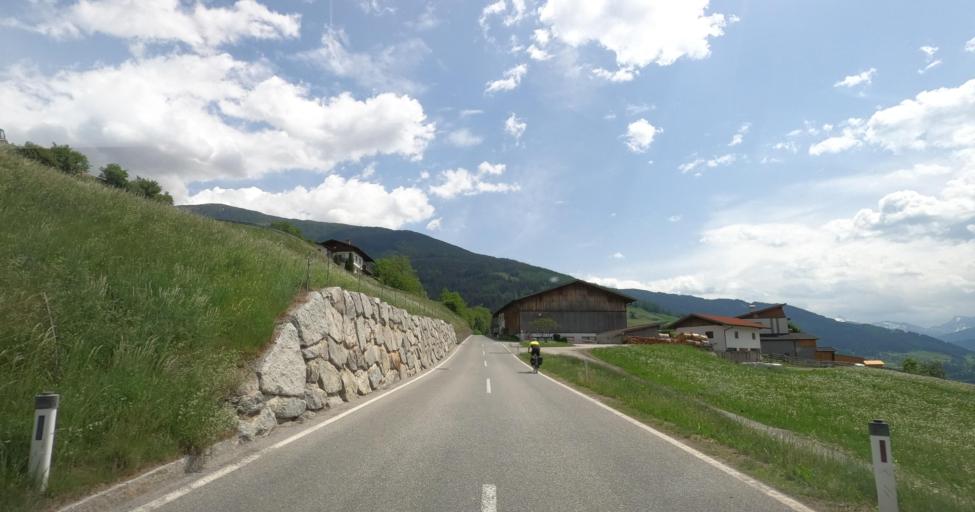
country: AT
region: Tyrol
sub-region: Politischer Bezirk Innsbruck Land
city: Ellbogen
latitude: 47.1655
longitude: 11.4487
